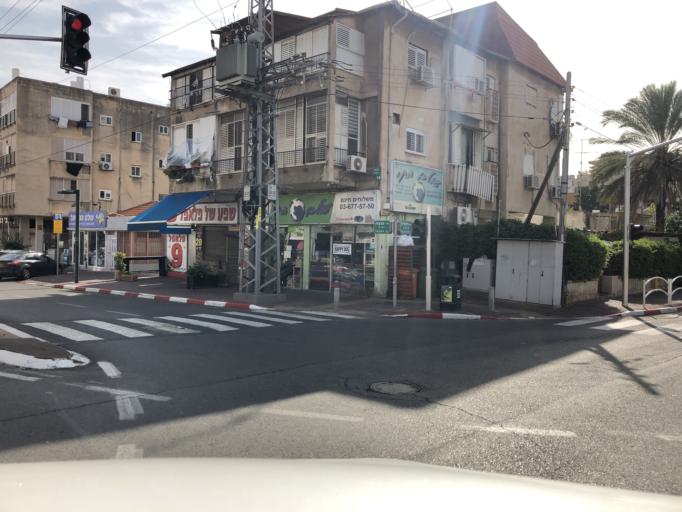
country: IL
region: Tel Aviv
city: Giv`atayim
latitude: 32.0705
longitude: 34.8247
